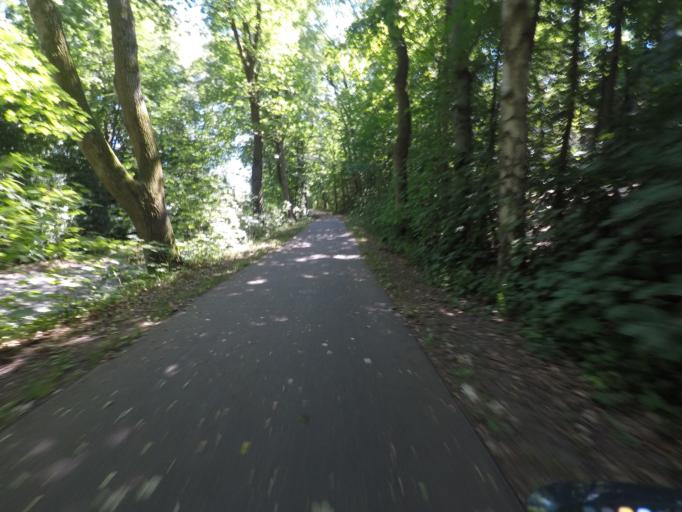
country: DE
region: Schleswig-Holstein
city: Lutjensee
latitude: 53.6390
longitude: 10.3735
